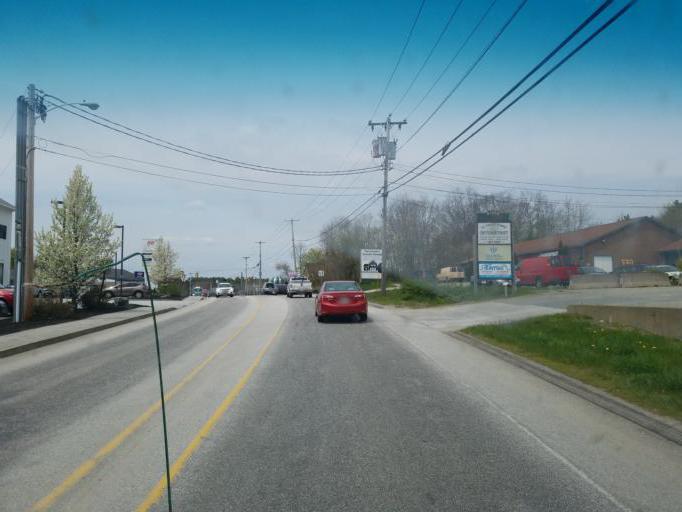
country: US
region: Maine
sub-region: Hancock County
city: Ellsworth
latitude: 44.5492
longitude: -68.4252
